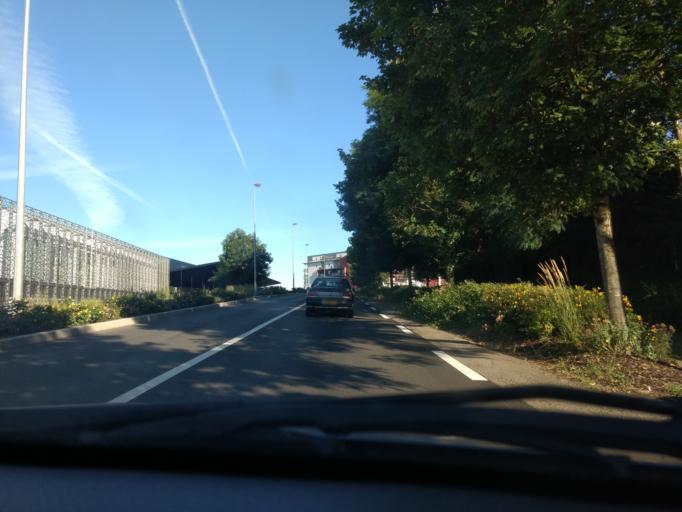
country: FR
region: Midi-Pyrenees
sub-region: Departement de l'Aveyron
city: Olemps
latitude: 44.3625
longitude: 2.5546
